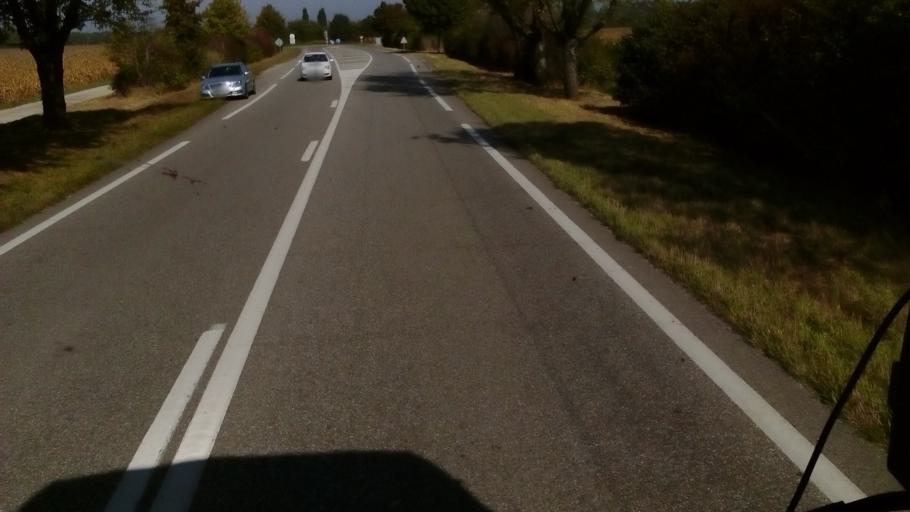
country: FR
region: Alsace
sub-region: Departement du Bas-Rhin
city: Gambsheim
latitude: 48.6985
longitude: 7.8998
